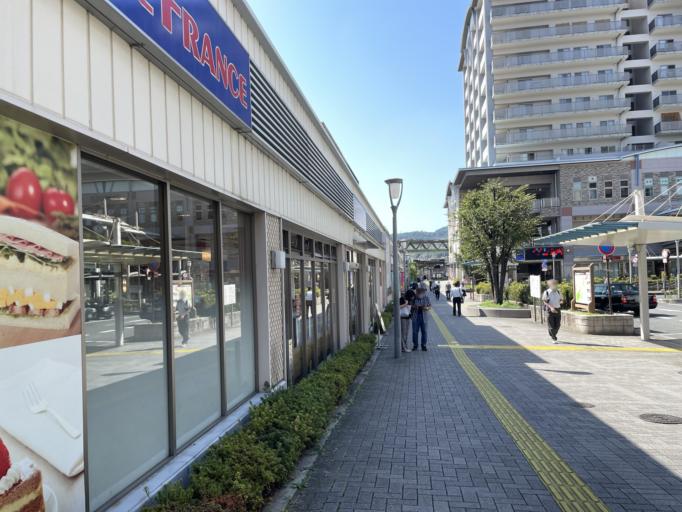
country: JP
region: Nara
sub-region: Ikoma-shi
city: Ikoma
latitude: 34.5977
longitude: 135.7038
